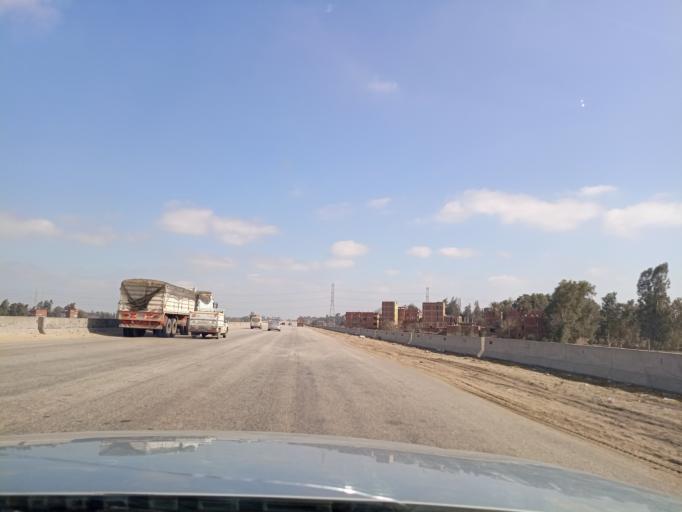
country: EG
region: Muhafazat al Minufiyah
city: Al Bajur
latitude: 30.4367
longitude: 31.1073
